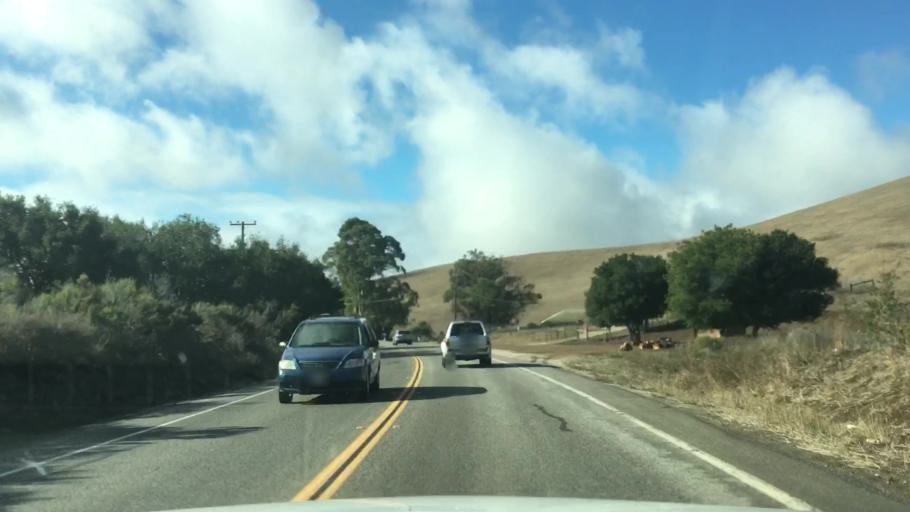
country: US
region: California
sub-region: San Luis Obispo County
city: Morro Bay
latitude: 35.4105
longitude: -120.8103
